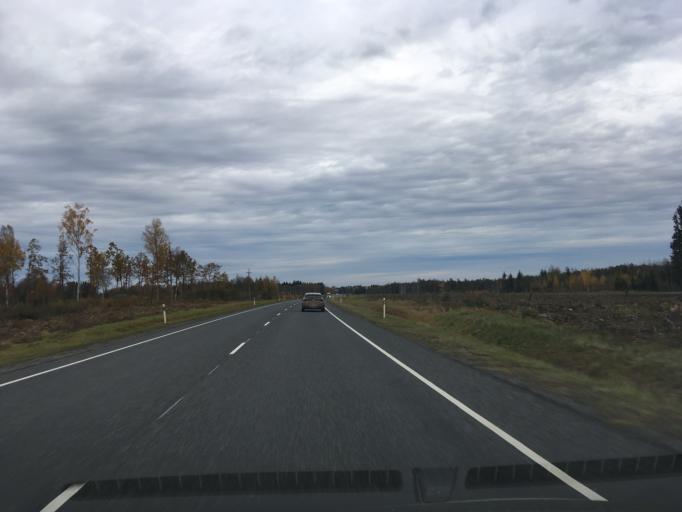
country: EE
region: Harju
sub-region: Nissi vald
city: Turba
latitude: 58.9814
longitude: 24.0576
